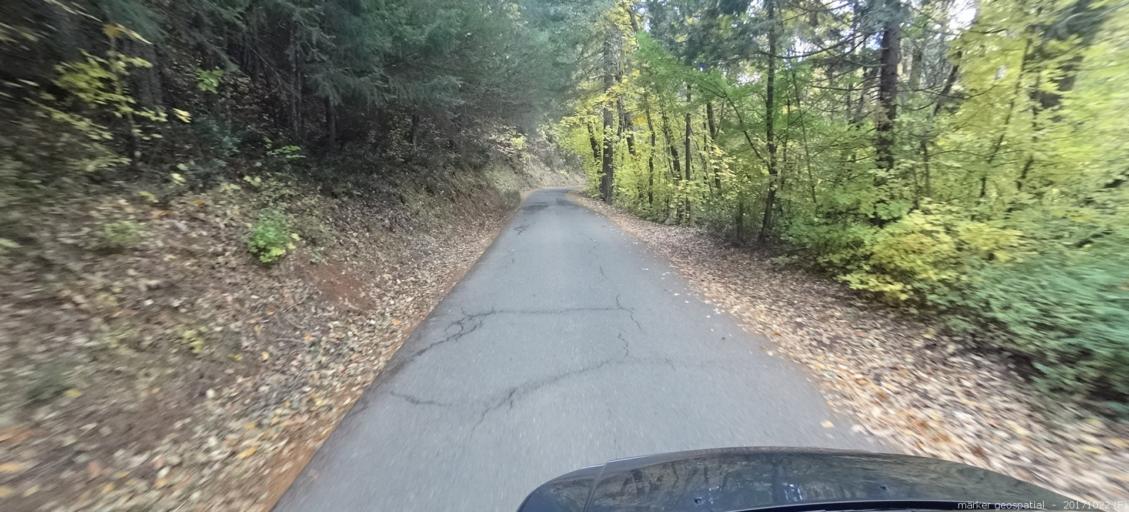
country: US
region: California
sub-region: Siskiyou County
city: Dunsmuir
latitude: 41.1704
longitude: -122.2770
